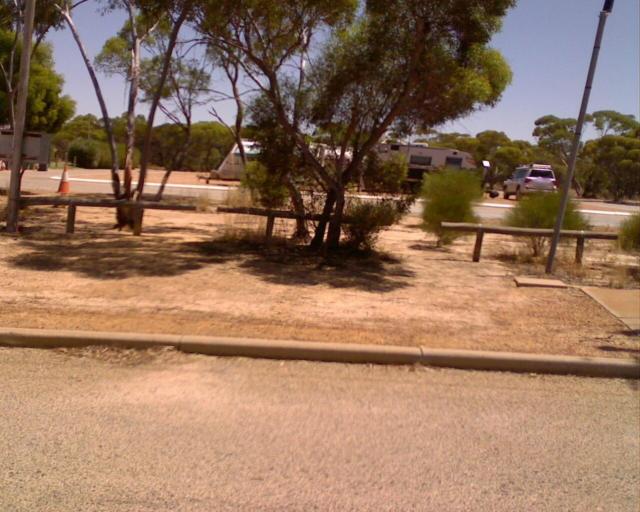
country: AU
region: Western Australia
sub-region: Wongan-Ballidu
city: Wongan Hills
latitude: -30.8224
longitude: 117.4869
